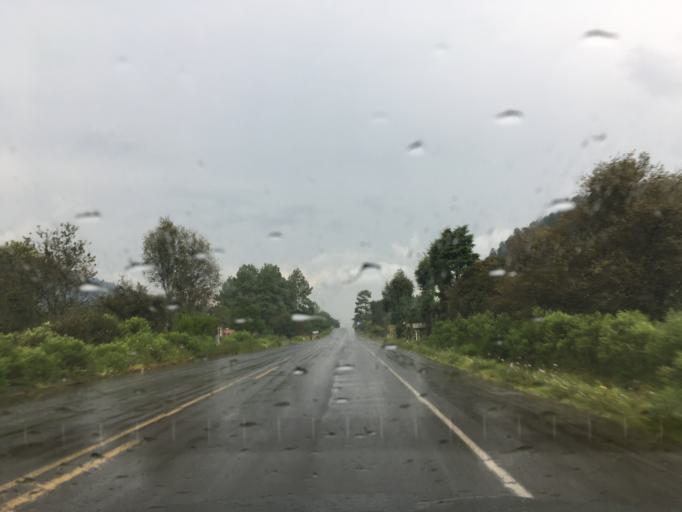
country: MX
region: Michoacan
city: Angahuan
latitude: 19.5603
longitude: -102.2275
